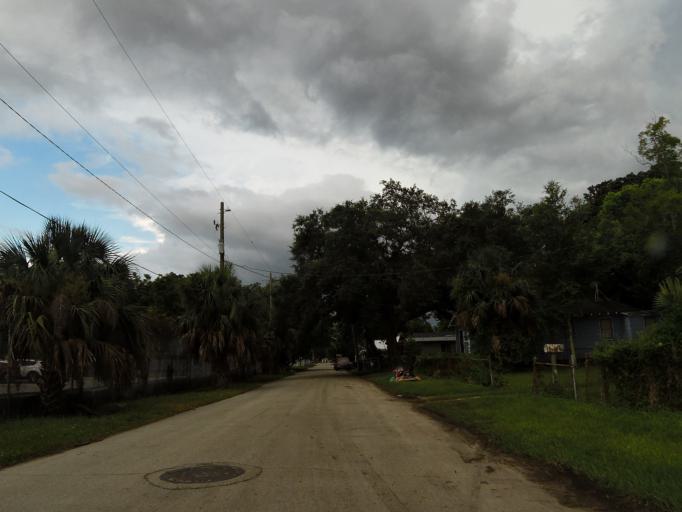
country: US
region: Florida
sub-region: Duval County
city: Jacksonville
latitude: 30.3473
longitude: -81.6305
